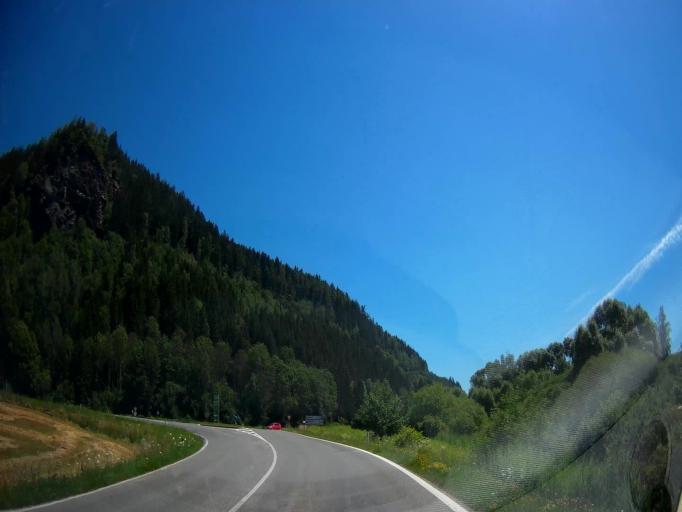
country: AT
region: Carinthia
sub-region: Politischer Bezirk Sankt Veit an der Glan
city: Micheldorf
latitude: 46.9012
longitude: 14.4390
